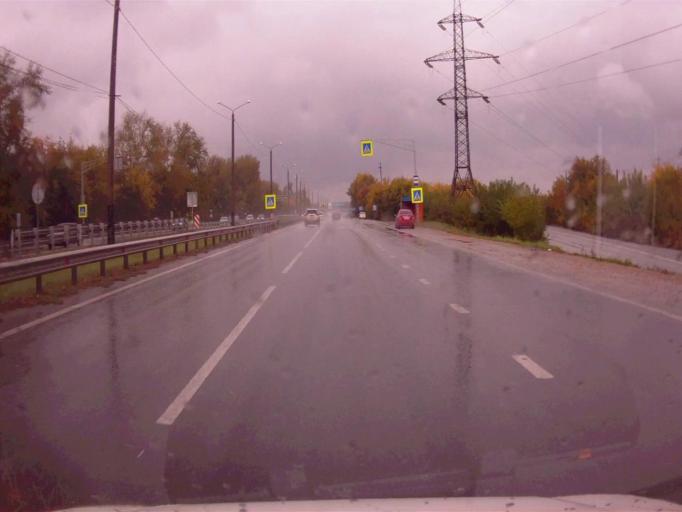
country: RU
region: Chelyabinsk
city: Dolgoderevenskoye
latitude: 55.2570
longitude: 61.3517
